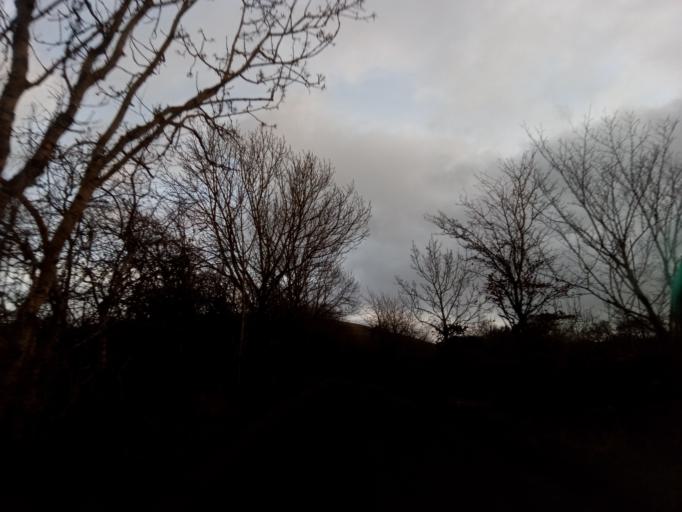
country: GB
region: Scotland
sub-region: The Scottish Borders
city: Selkirk
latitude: 55.5657
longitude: -2.8024
